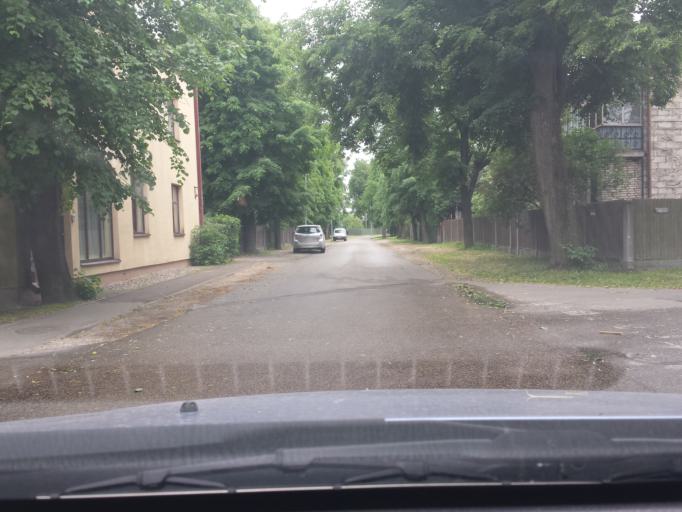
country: LV
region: Riga
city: Jaunciems
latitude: 56.9730
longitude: 24.1843
